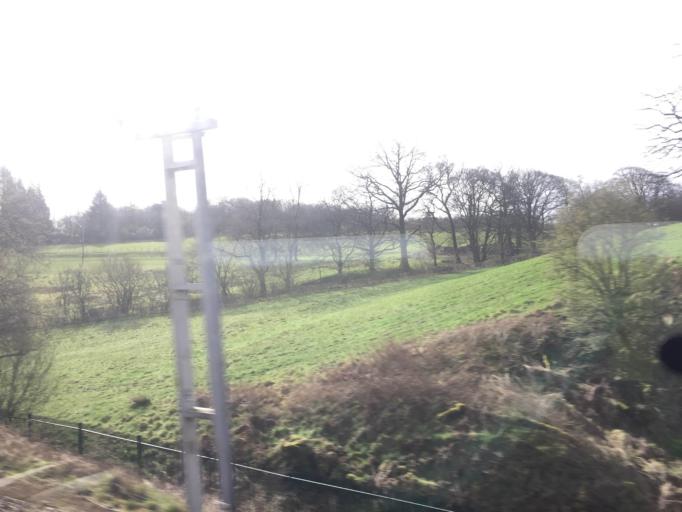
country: GB
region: England
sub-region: Cumbria
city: Kendal
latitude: 54.3596
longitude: -2.6417
